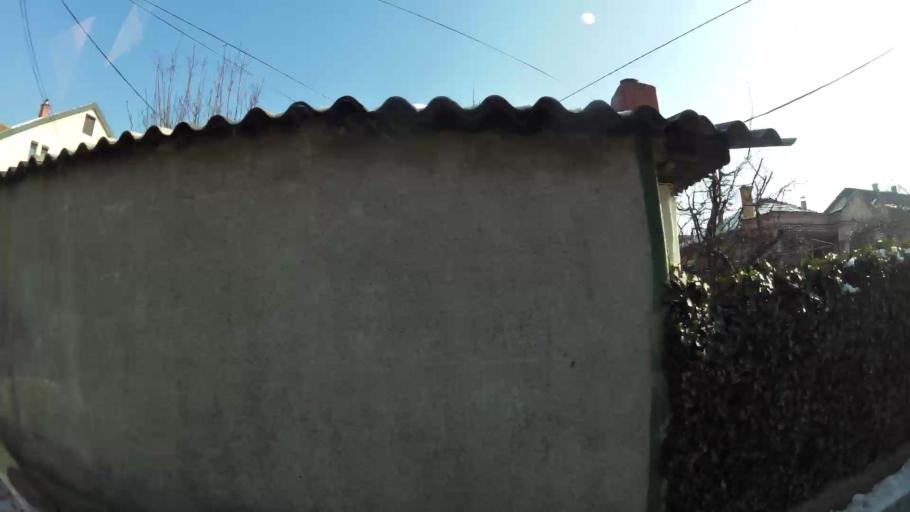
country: MK
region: Kisela Voda
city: Usje
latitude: 41.9714
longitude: 21.4496
